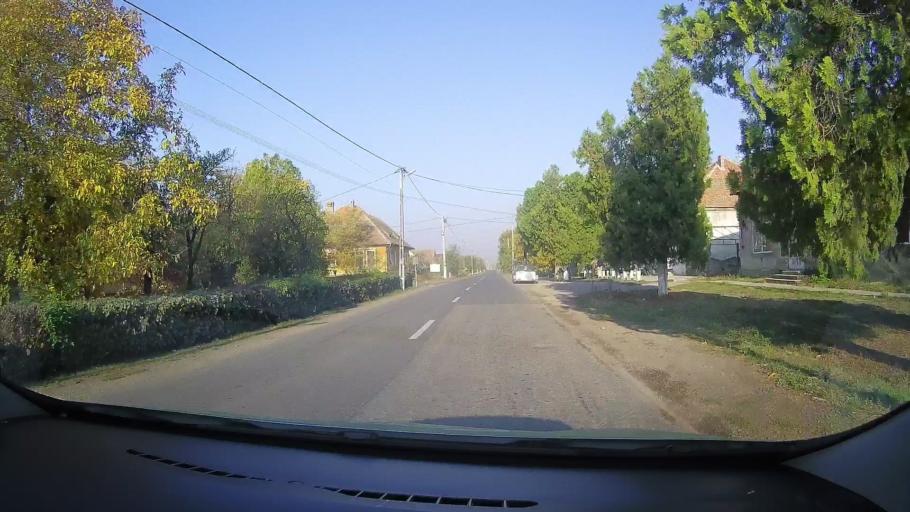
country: RO
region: Arad
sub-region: Comuna Graniceri
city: Siclau
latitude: 46.4934
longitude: 21.3661
